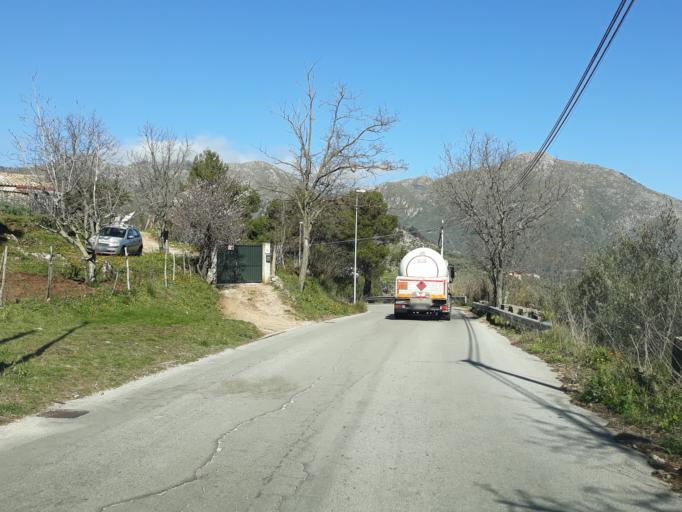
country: IT
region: Sicily
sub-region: Palermo
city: Piano dei Geli
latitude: 38.0840
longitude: 13.2683
